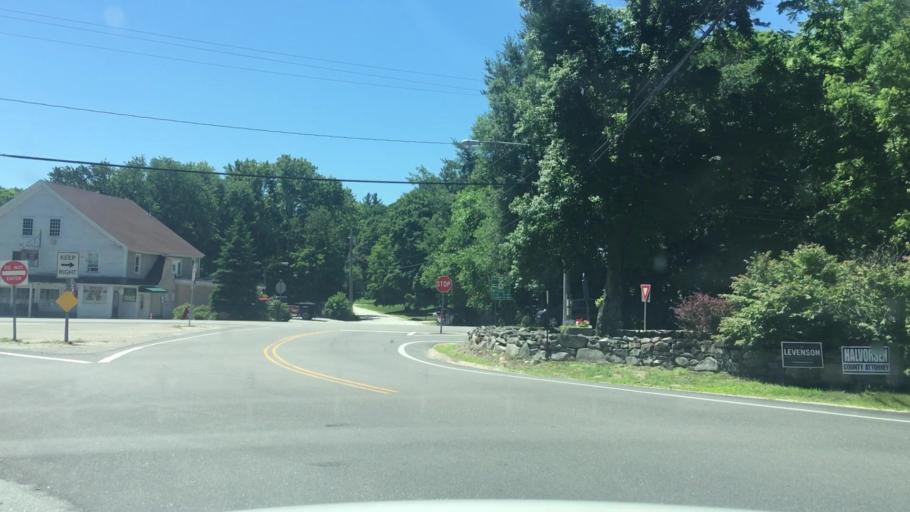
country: US
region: New Hampshire
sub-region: Merrimack County
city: Hopkinton
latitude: 43.1919
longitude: -71.6748
